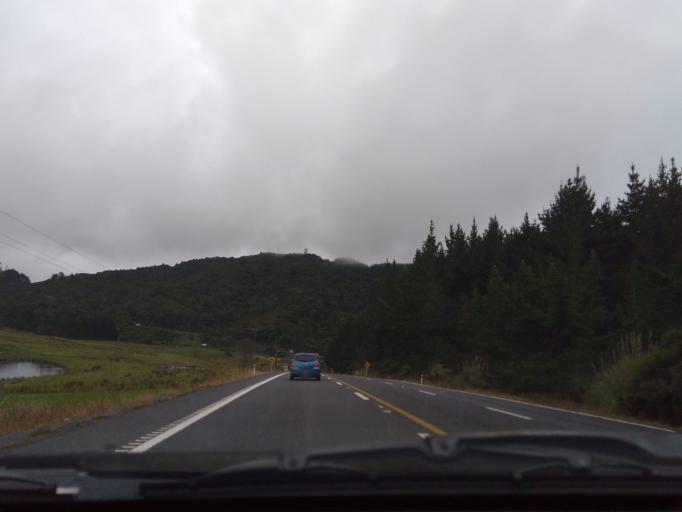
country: NZ
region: Northland
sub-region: Whangarei
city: Ruakaka
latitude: -36.0848
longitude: 174.4302
